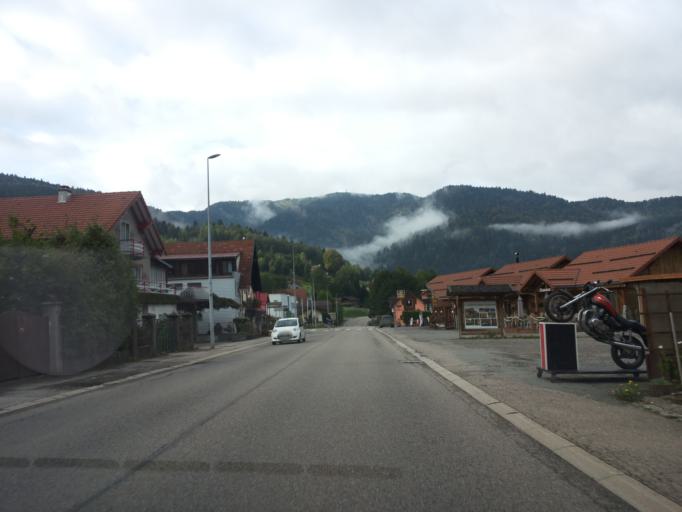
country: FR
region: Lorraine
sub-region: Departement des Vosges
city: Saint-Maurice-sur-Moselle
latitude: 47.8562
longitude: 6.8207
